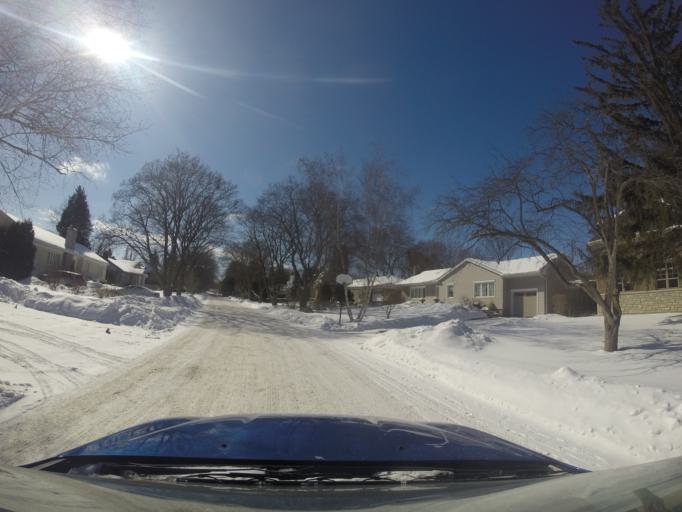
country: CA
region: Ontario
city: Burlington
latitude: 43.3413
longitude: -79.7708
